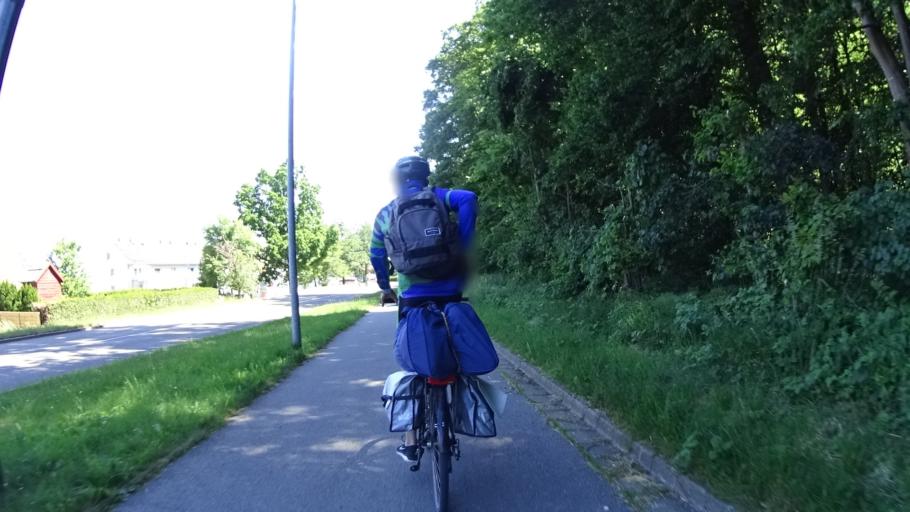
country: DE
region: Bavaria
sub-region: Regierungsbezirk Mittelfranken
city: Gunzenhausen
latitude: 49.1194
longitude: 10.7824
